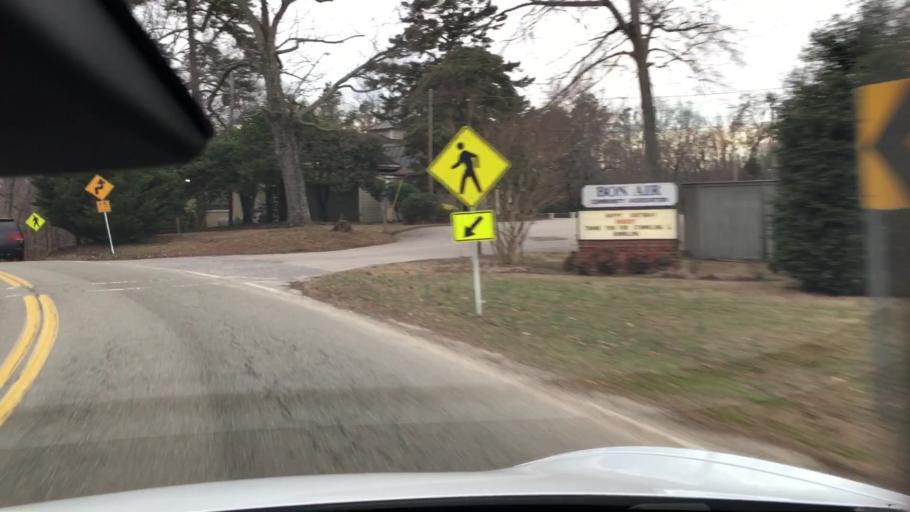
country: US
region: Virginia
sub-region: Chesterfield County
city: Bon Air
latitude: 37.5244
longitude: -77.5597
